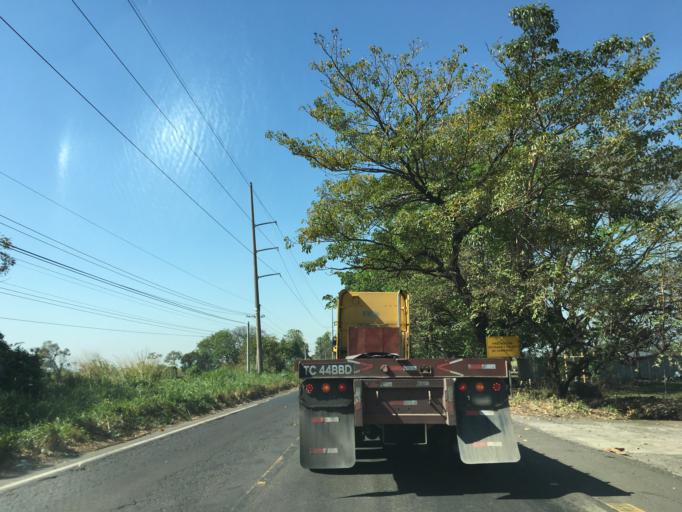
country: GT
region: Escuintla
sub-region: Municipio de Escuintla
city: Escuintla
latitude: 14.2496
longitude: -90.8063
